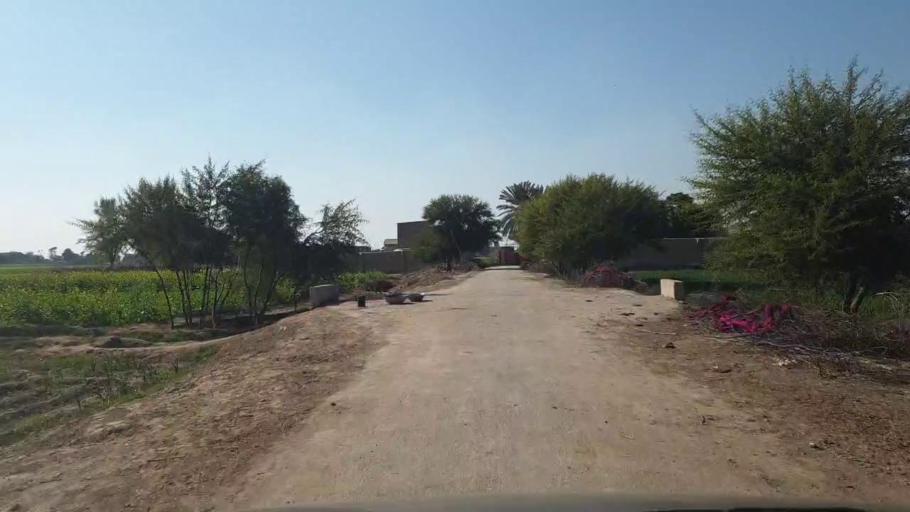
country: PK
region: Sindh
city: Shahpur Chakar
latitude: 26.1035
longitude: 68.6446
